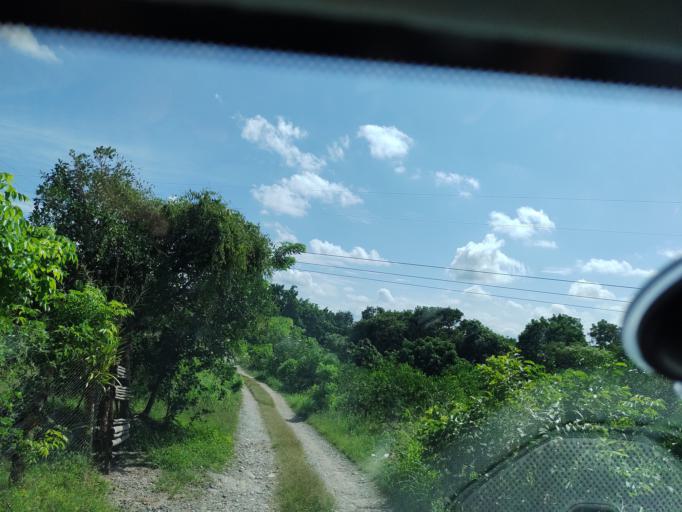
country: MX
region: Veracruz
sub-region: Martinez de la Torre
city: El Progreso
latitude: 20.1131
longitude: -97.0098
